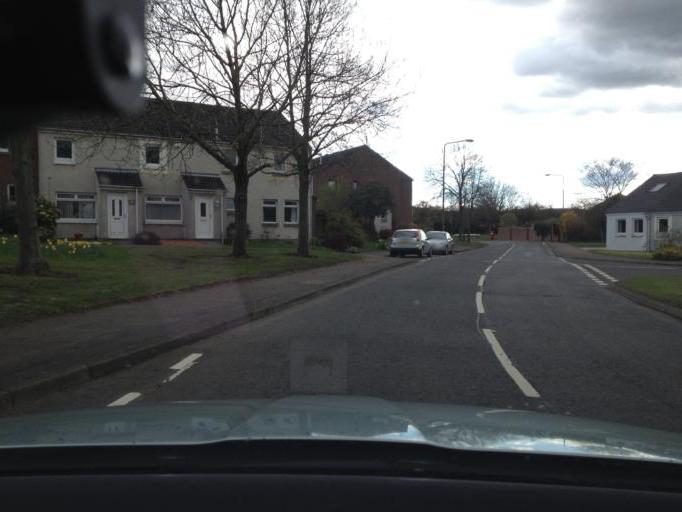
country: GB
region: Scotland
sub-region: West Lothian
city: Linlithgow
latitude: 55.9831
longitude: -3.5738
